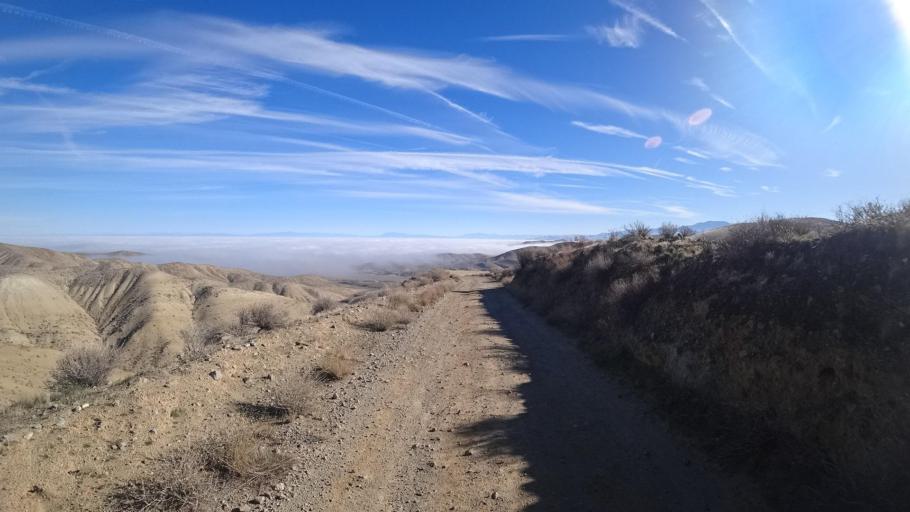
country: US
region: California
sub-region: Kern County
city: Maricopa
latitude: 35.0126
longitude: -119.4667
